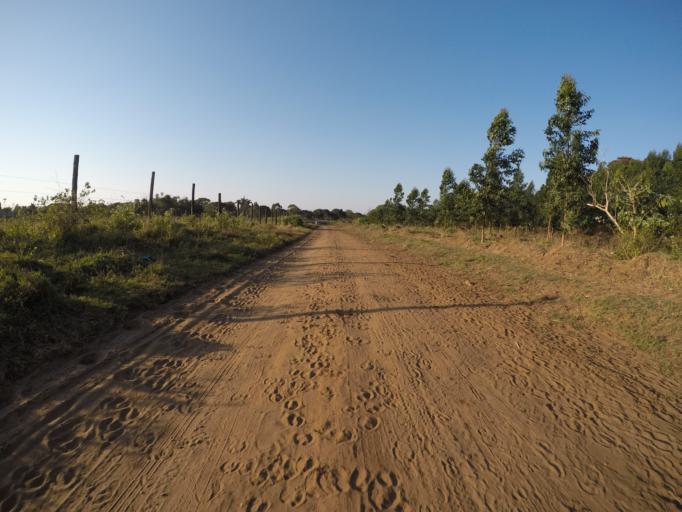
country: ZA
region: KwaZulu-Natal
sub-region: uThungulu District Municipality
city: KwaMbonambi
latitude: -28.6926
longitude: 32.2007
